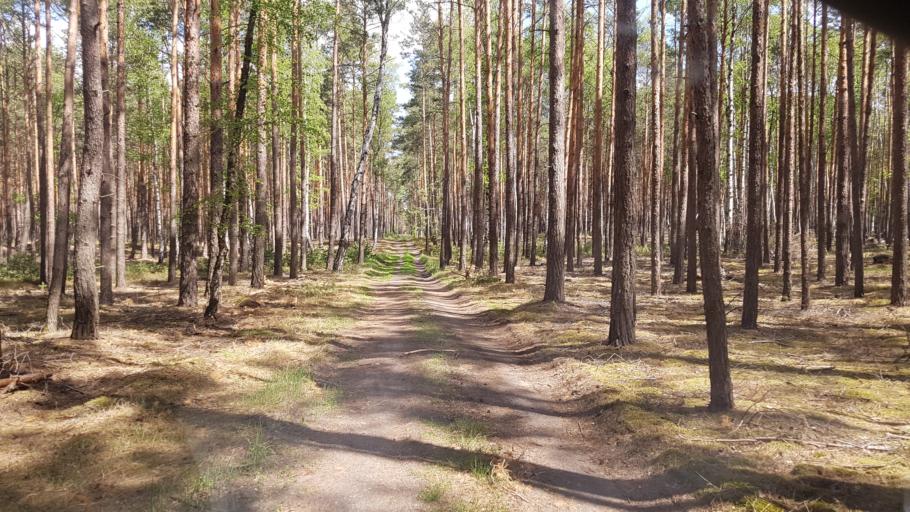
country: DE
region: Brandenburg
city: Sonnewalde
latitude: 51.6476
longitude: 13.6599
